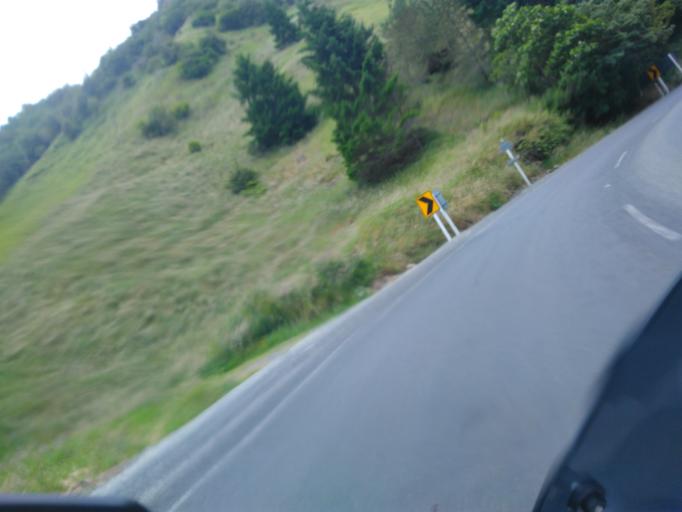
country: NZ
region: Bay of Plenty
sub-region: Opotiki District
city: Opotiki
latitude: -38.3449
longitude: 177.4527
